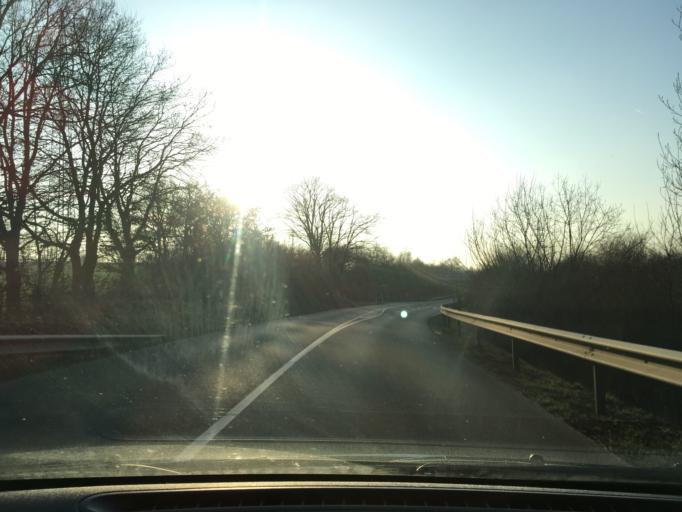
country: DE
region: Lower Saxony
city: Barum
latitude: 53.0622
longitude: 10.5376
